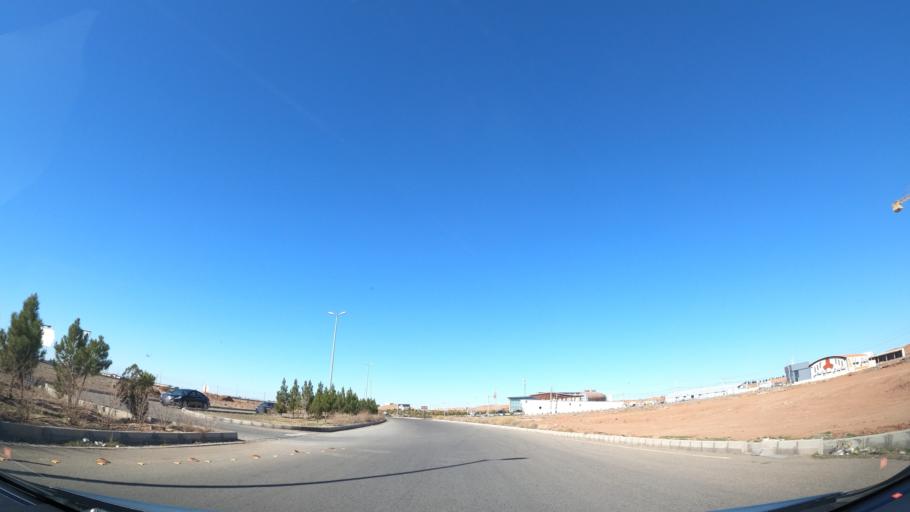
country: IR
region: Qom
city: Qom
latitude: 34.7407
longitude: 50.8668
